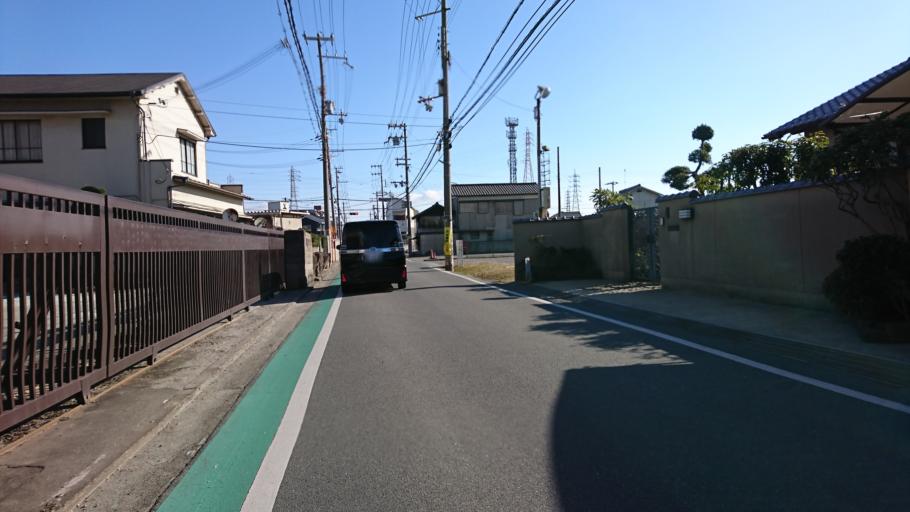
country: JP
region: Hyogo
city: Kakogawacho-honmachi
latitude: 34.7255
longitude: 134.8497
